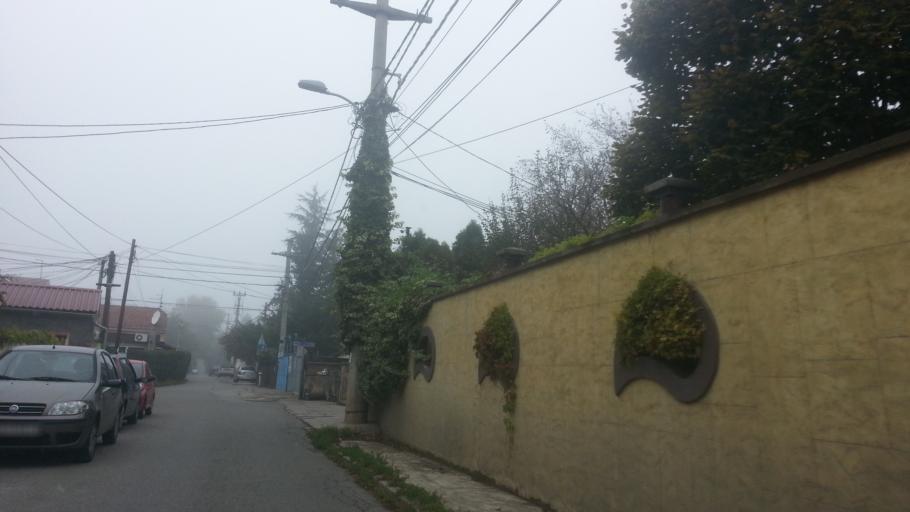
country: RS
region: Central Serbia
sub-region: Belgrade
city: Zemun
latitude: 44.8578
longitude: 20.3847
